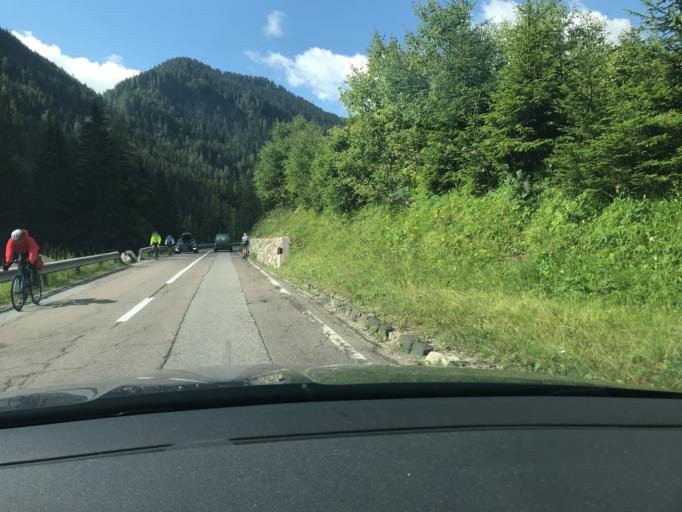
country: IT
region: Trentino-Alto Adige
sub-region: Bolzano
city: Corvara in Badia
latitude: 46.5704
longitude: 11.8908
